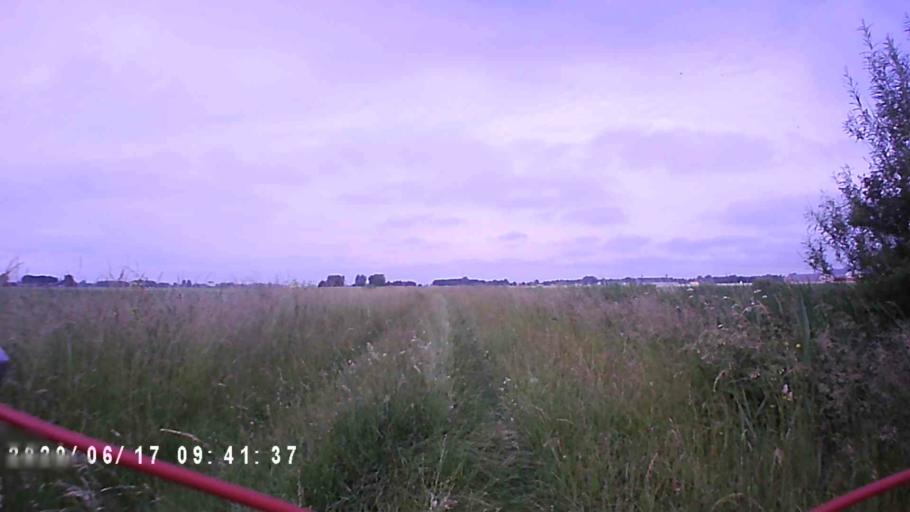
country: NL
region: Groningen
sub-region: Gemeente De Marne
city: Ulrum
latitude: 53.3525
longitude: 6.3567
